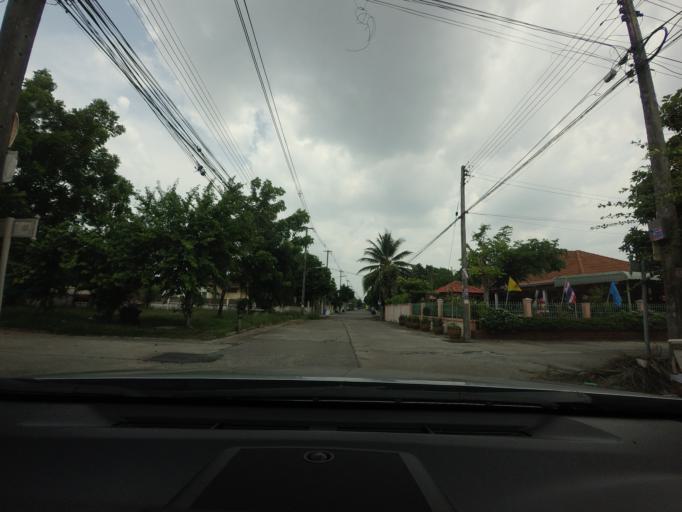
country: TH
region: Nakhon Si Thammarat
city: Nakhon Si Thammarat
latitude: 8.4490
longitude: 99.9967
